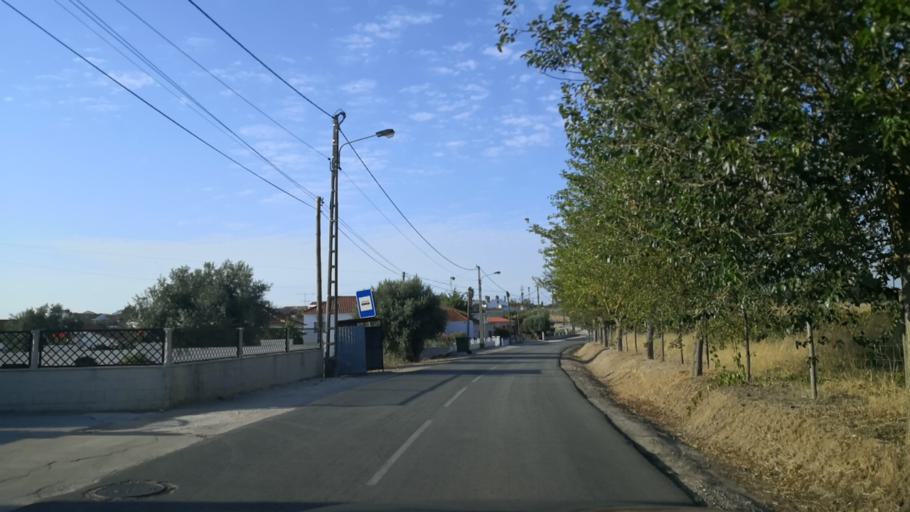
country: PT
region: Santarem
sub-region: Santarem
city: Santarem
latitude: 39.2873
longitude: -8.6542
